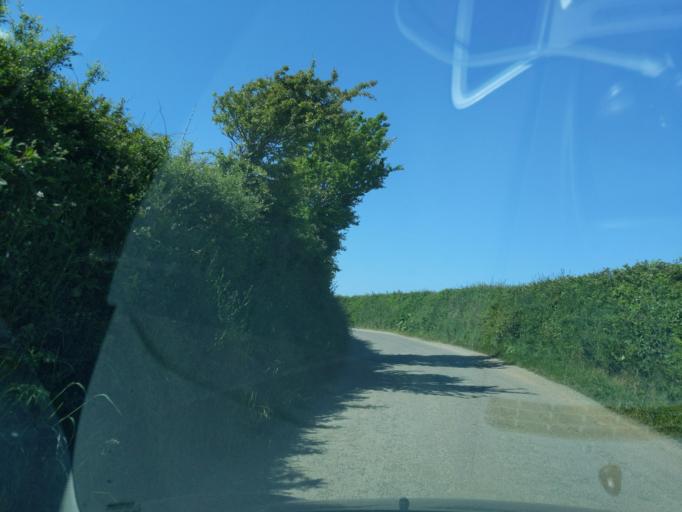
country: GB
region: England
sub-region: Cornwall
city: Wadebridge
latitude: 50.5771
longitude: -4.8306
